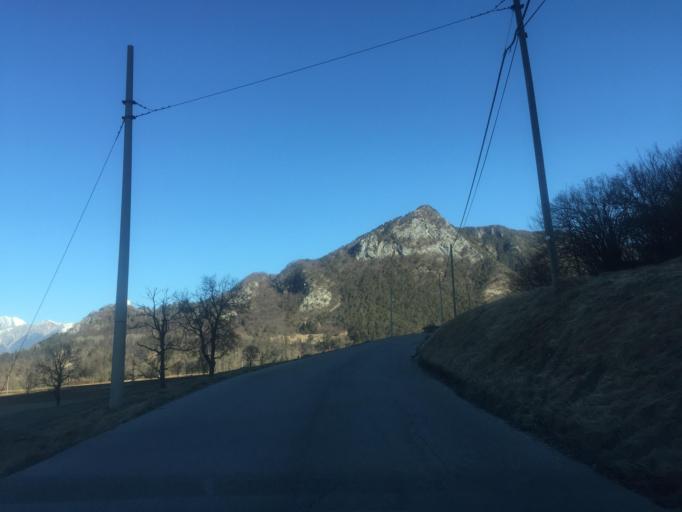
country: IT
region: Friuli Venezia Giulia
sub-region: Provincia di Udine
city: Tolmezzo
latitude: 46.4229
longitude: 13.0516
